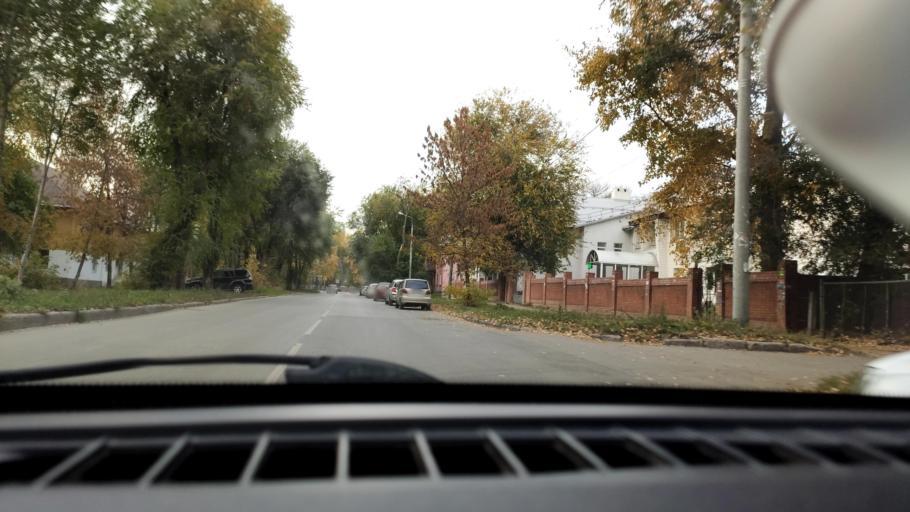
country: RU
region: Samara
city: Samara
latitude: 53.2304
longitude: 50.2622
